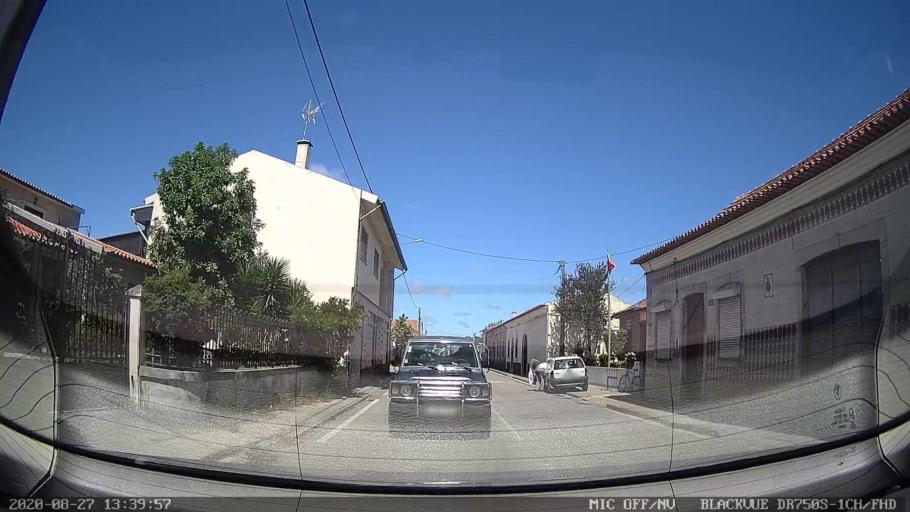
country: PT
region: Coimbra
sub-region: Mira
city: Mira
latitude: 40.4374
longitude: -8.7282
